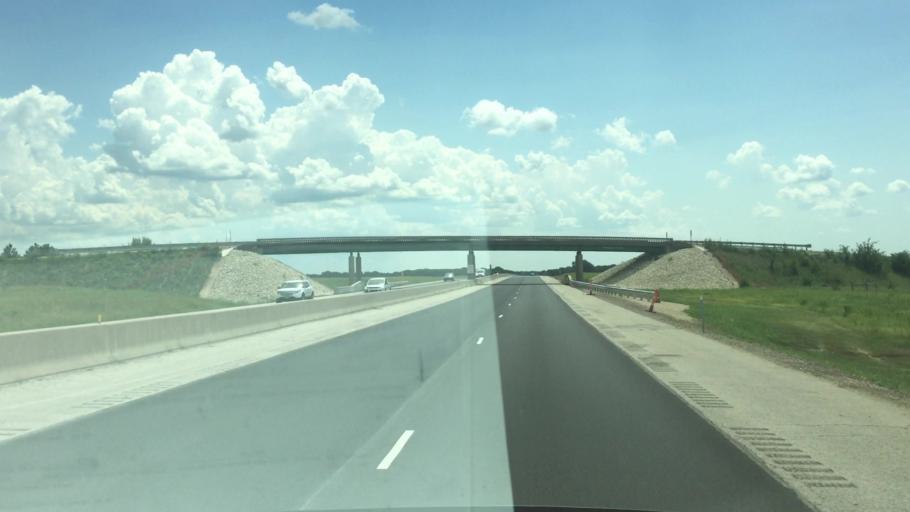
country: US
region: Kansas
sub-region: Lyon County
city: Emporia
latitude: 38.5364
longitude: -96.1341
